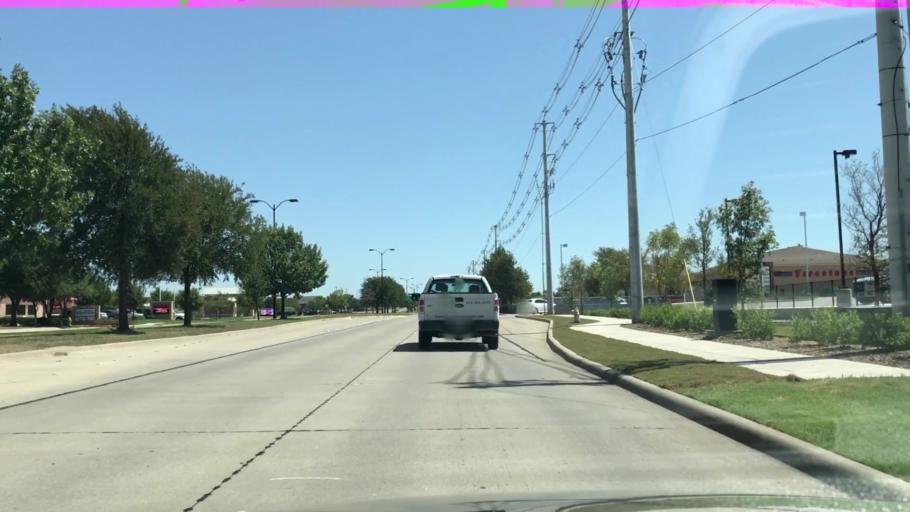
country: US
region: Texas
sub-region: Collin County
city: Frisco
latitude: 33.1531
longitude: -96.8685
